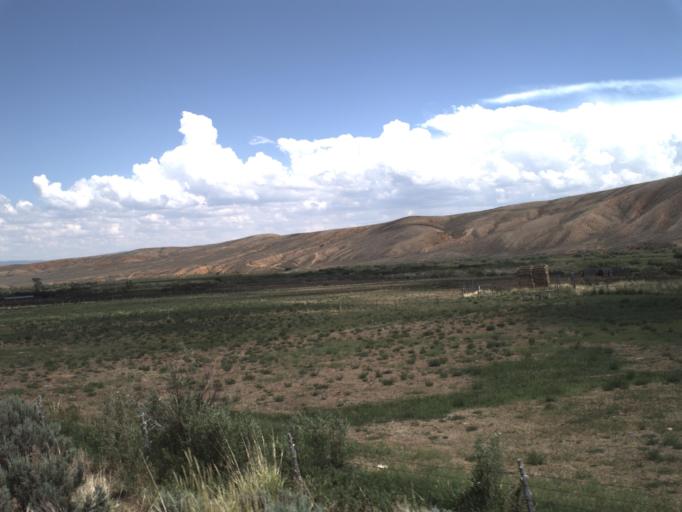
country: US
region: Utah
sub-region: Rich County
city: Randolph
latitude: 41.5007
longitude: -111.2492
